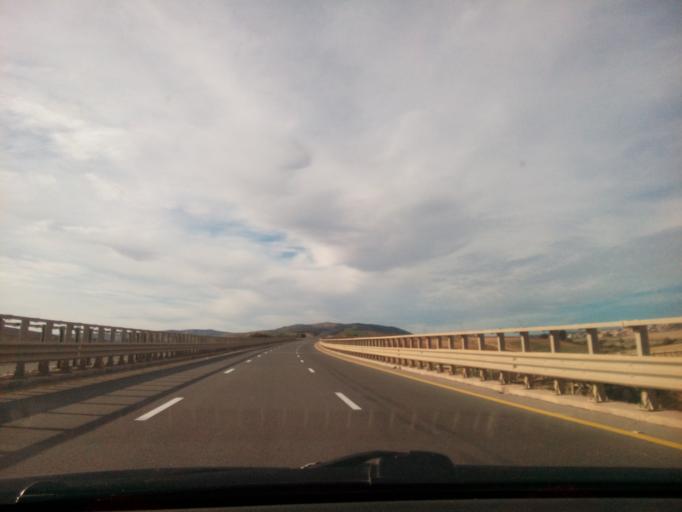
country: DZ
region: Sidi Bel Abbes
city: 'Ain el Berd
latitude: 35.4556
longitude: -0.3893
